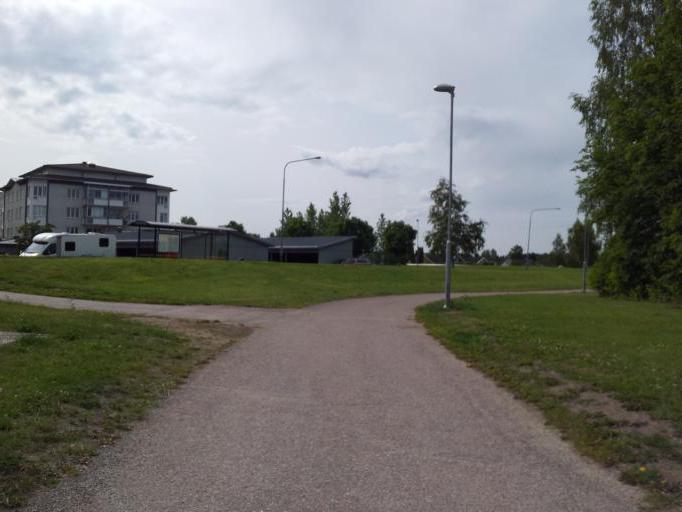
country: SE
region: Uppsala
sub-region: Uppsala Kommun
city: Gamla Uppsala
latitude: 59.8898
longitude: 17.6460
